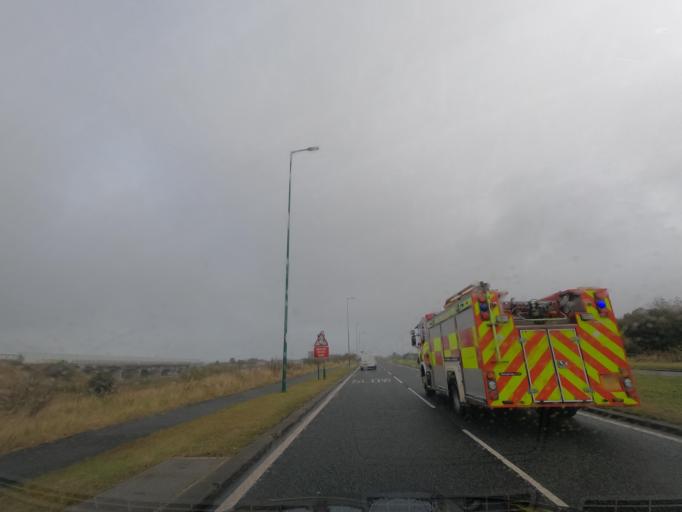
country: GB
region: England
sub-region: Redcar and Cleveland
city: South Bank
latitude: 54.6032
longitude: -1.1152
